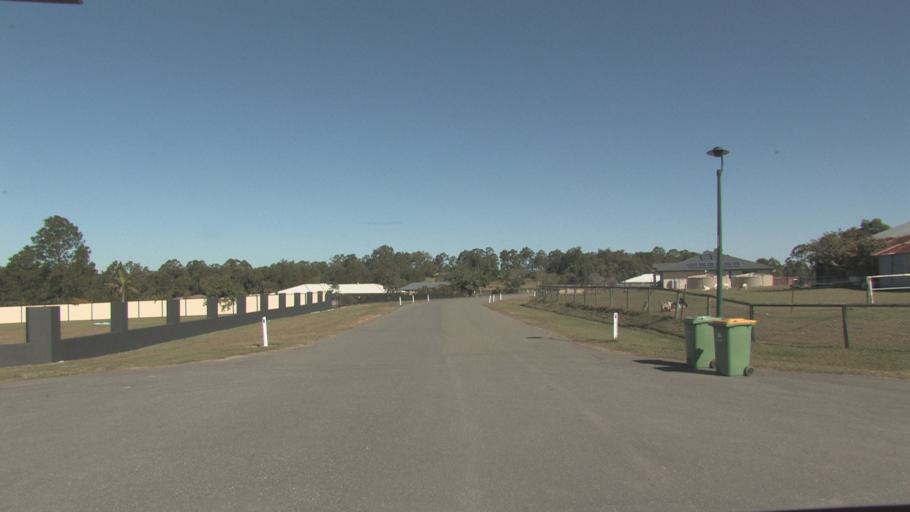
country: AU
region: Queensland
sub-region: Logan
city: Logan Reserve
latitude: -27.7254
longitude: 153.1234
